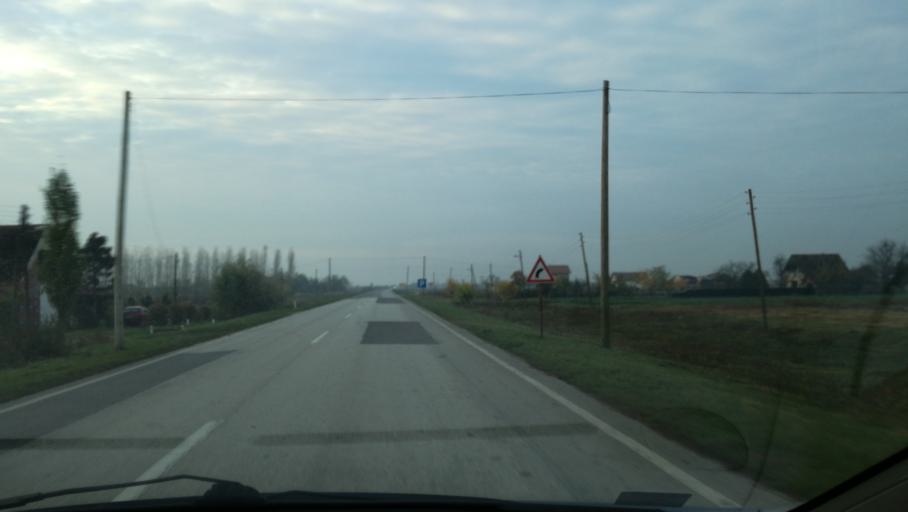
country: RS
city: Basaid
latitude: 45.6784
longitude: 20.4228
